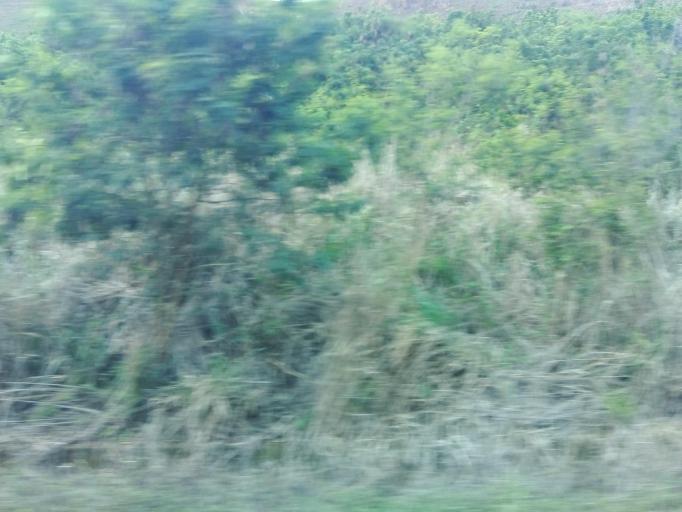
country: BR
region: Minas Gerais
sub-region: Governador Valadares
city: Governador Valadares
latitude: -18.9249
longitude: -42.0216
